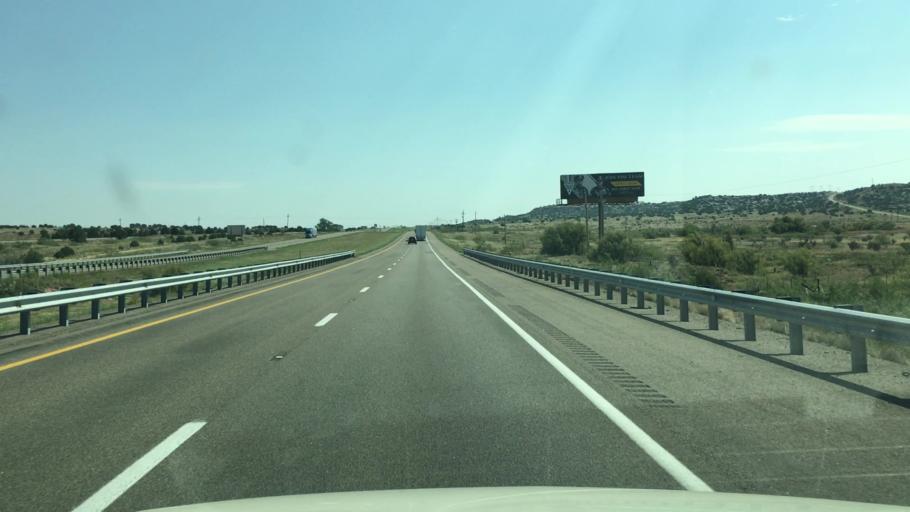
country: US
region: New Mexico
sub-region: Guadalupe County
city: Santa Rosa
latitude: 34.9528
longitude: -104.6286
